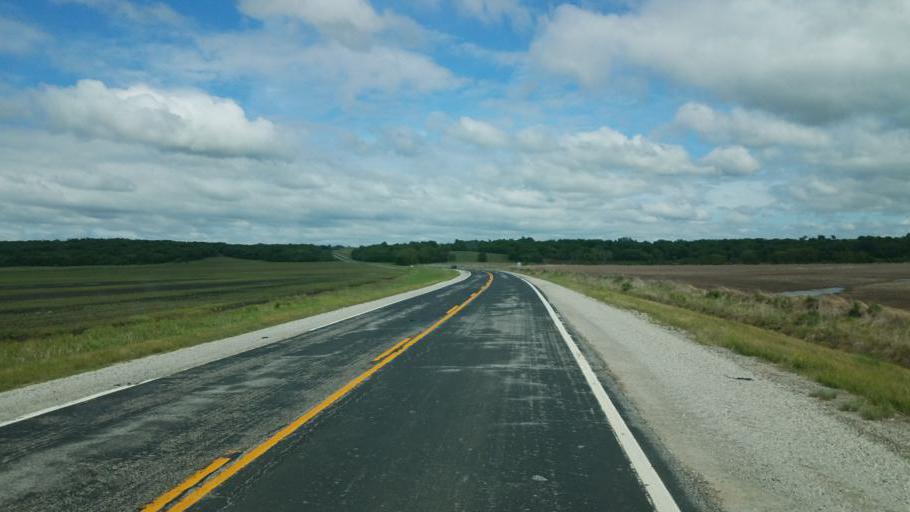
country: US
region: Missouri
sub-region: Mercer County
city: Princeton
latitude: 40.3364
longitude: -93.7633
